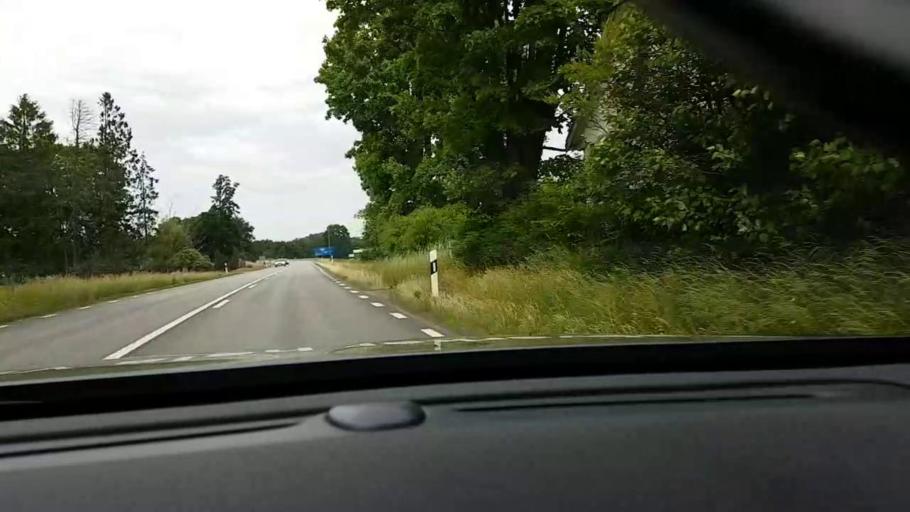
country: SE
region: Skane
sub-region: Hassleholms Kommun
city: Hassleholm
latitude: 56.1343
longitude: 13.7999
